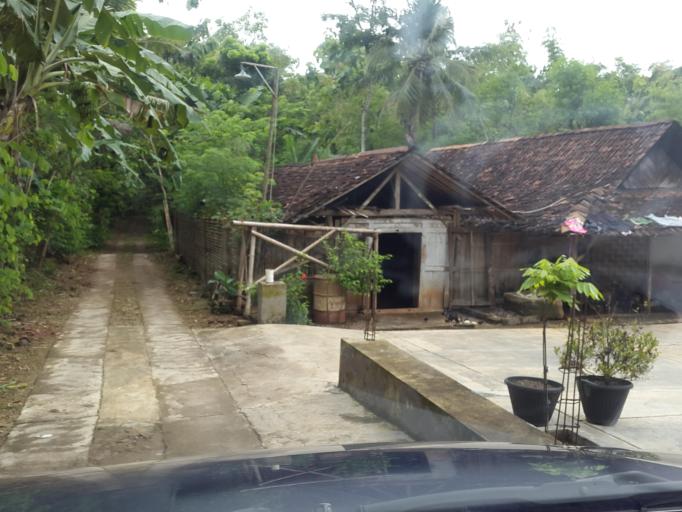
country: ID
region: Daerah Istimewa Yogyakarta
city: Wonosari
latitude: -7.9267
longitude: 110.6748
